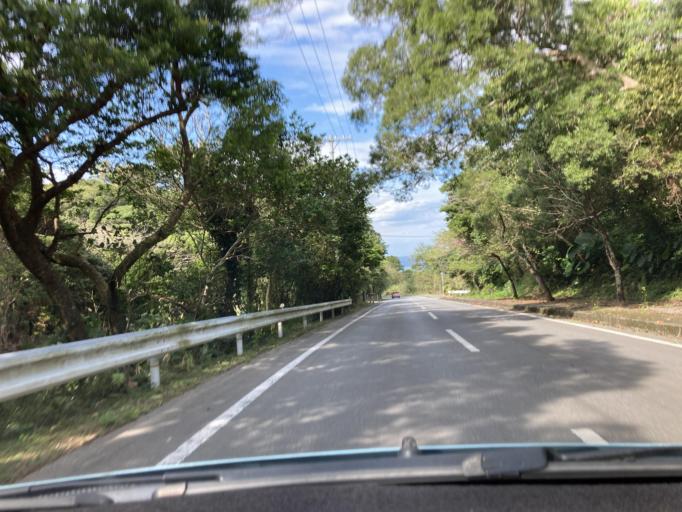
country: JP
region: Okinawa
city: Nago
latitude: 26.6936
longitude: 127.9251
